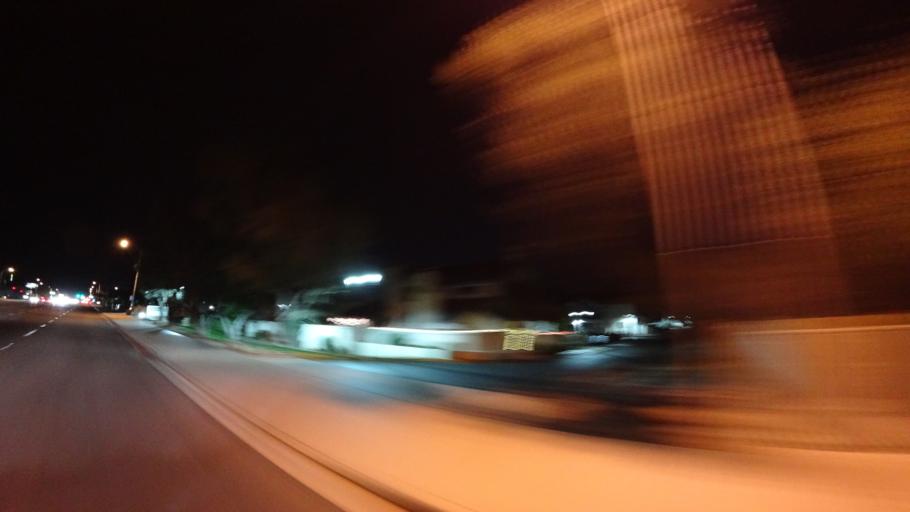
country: US
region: Arizona
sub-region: Maricopa County
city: Guadalupe
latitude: 33.3784
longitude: -111.9569
